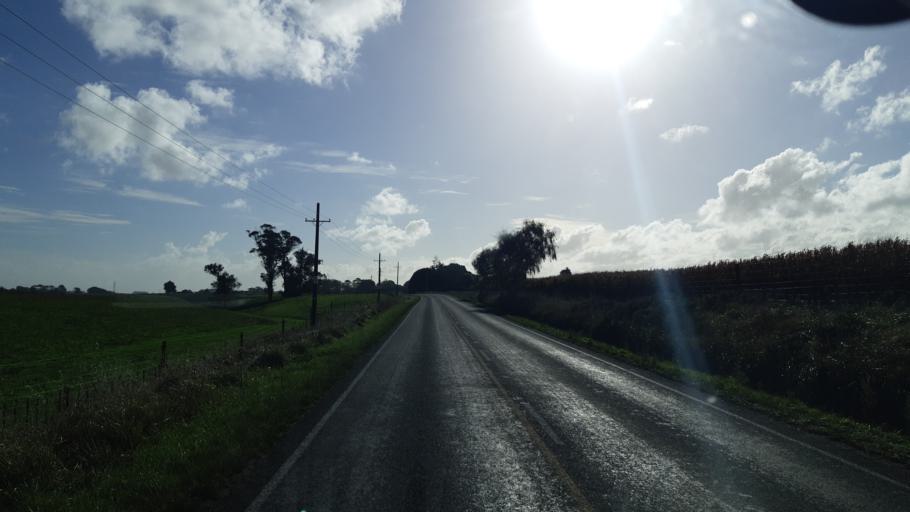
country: NZ
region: Manawatu-Wanganui
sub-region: Wanganui District
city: Wanganui
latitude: -39.9559
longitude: 175.1715
